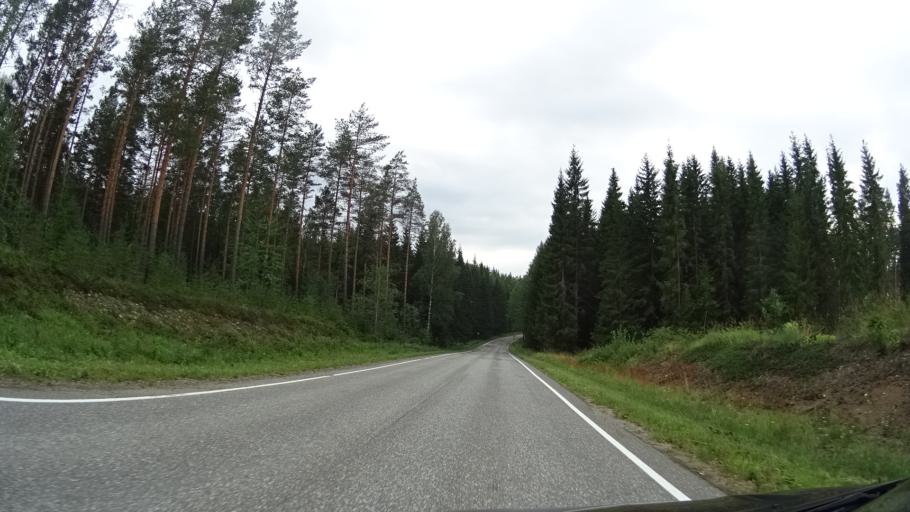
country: FI
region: Southern Savonia
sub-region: Savonlinna
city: Punkaharju
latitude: 61.7520
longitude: 29.4416
